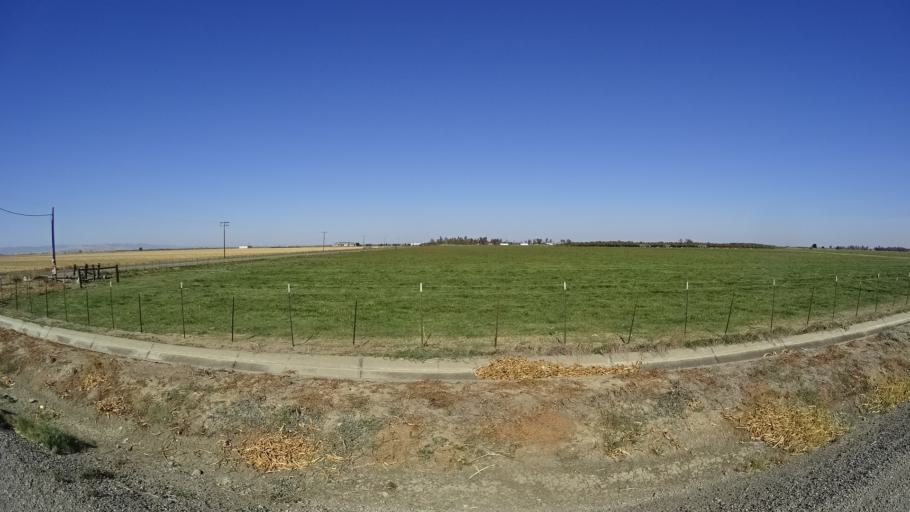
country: US
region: California
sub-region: Yolo County
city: Cottonwood
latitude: 38.6200
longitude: -121.8947
